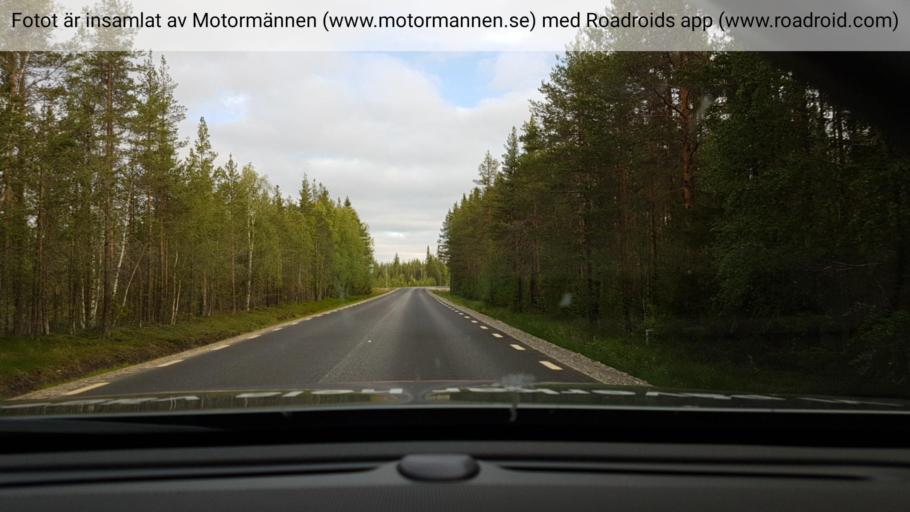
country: SE
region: Vaesterbotten
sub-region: Norsjo Kommun
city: Norsjoe
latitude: 64.4728
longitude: 19.3260
